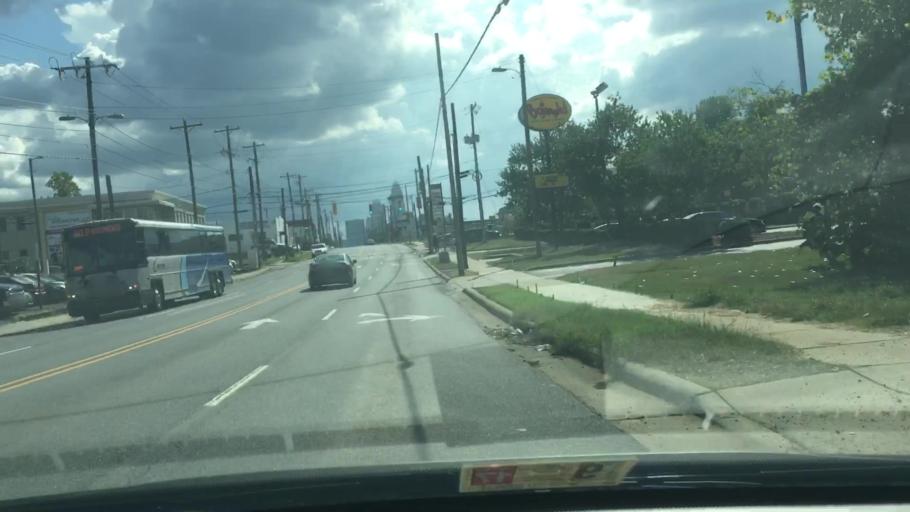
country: US
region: North Carolina
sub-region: Mecklenburg County
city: Charlotte
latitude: 35.2477
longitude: -80.8173
